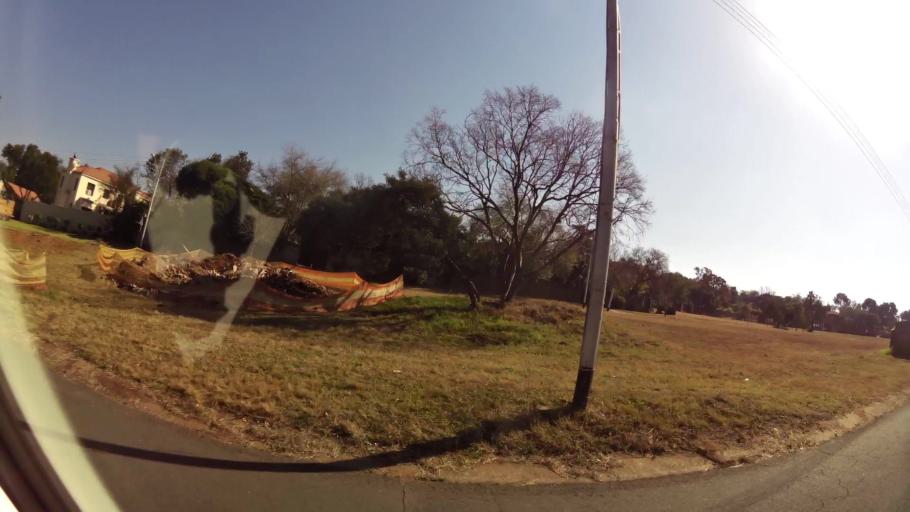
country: ZA
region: Gauteng
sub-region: City of Tshwane Metropolitan Municipality
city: Pretoria
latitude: -25.7734
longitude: 28.2714
